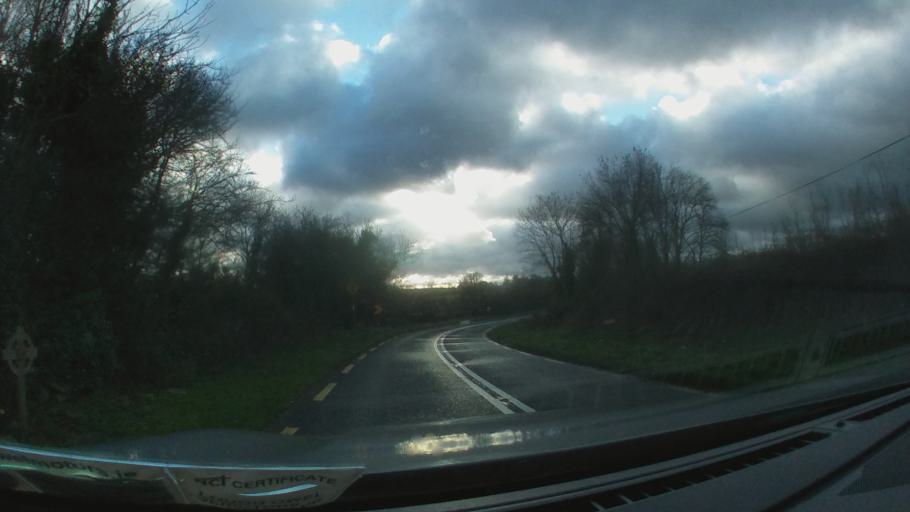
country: IE
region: Leinster
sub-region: Kilkenny
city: Thomastown
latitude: 52.5623
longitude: -7.1204
